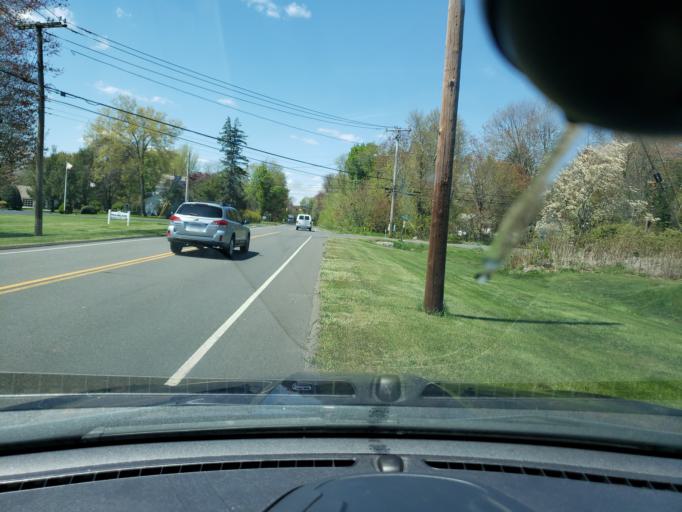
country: US
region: Connecticut
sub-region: New Haven County
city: Orange
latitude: 41.2839
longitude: -73.0104
